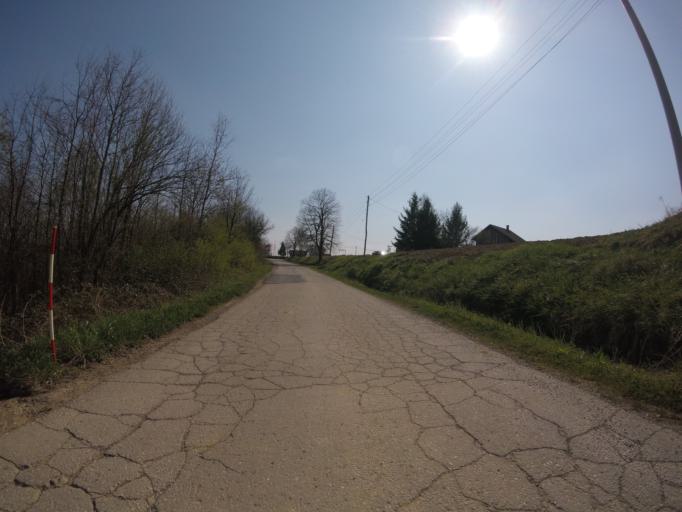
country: HR
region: Grad Zagreb
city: Strmec
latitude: 45.5552
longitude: 15.9022
